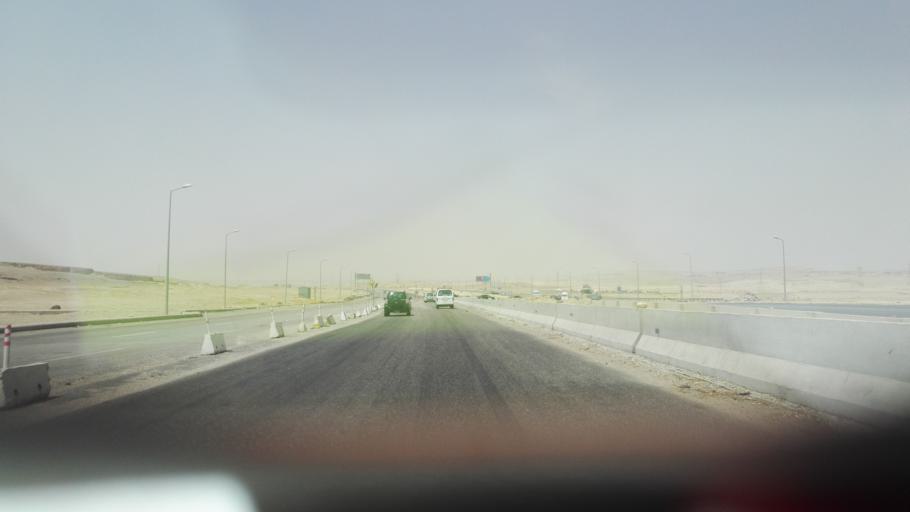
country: EG
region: As Suways
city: Ain Sukhna
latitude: 29.7591
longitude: 32.0118
